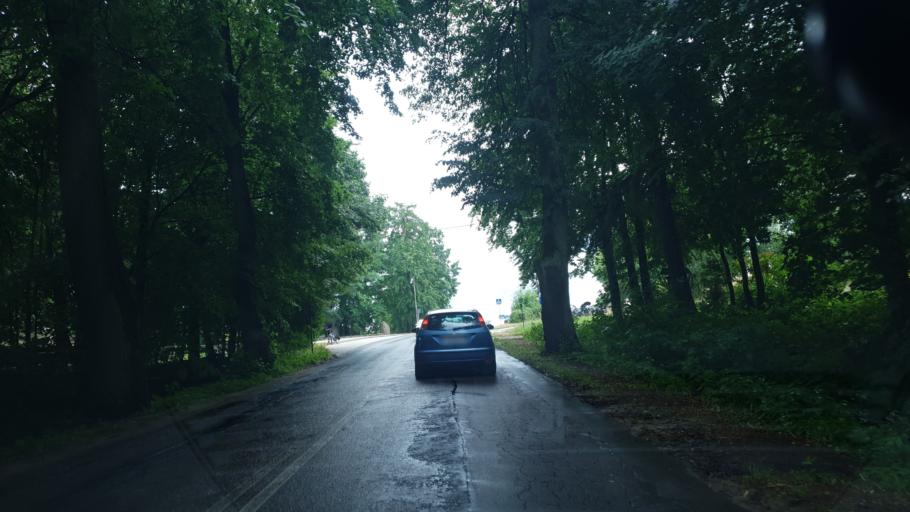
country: PL
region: Pomeranian Voivodeship
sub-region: Powiat kartuski
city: Chmielno
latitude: 54.2753
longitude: 18.0953
